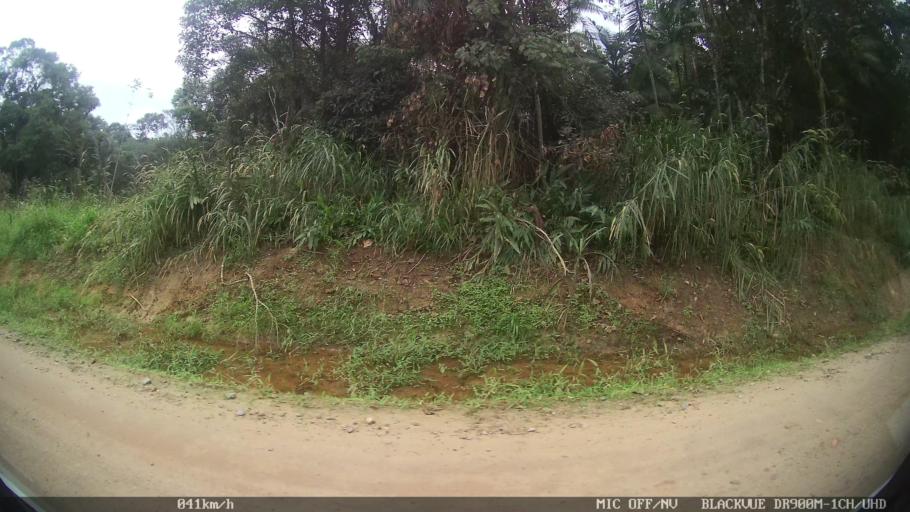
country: BR
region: Santa Catarina
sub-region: Joinville
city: Joinville
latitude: -26.2683
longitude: -48.9321
